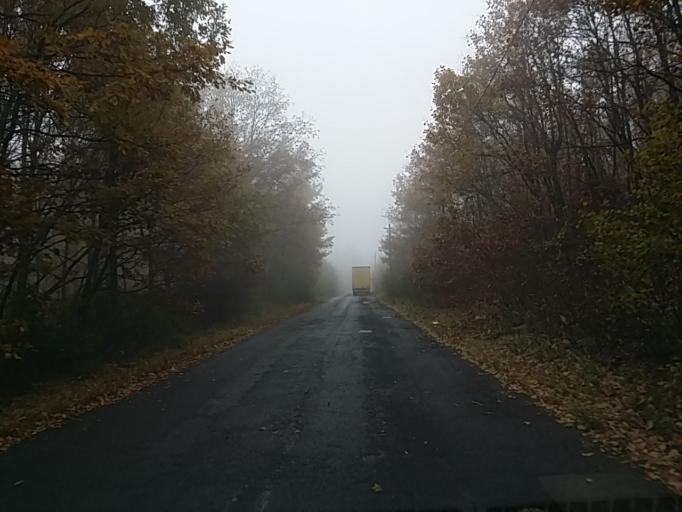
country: HU
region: Heves
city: Abasar
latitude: 47.8072
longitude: 19.9759
